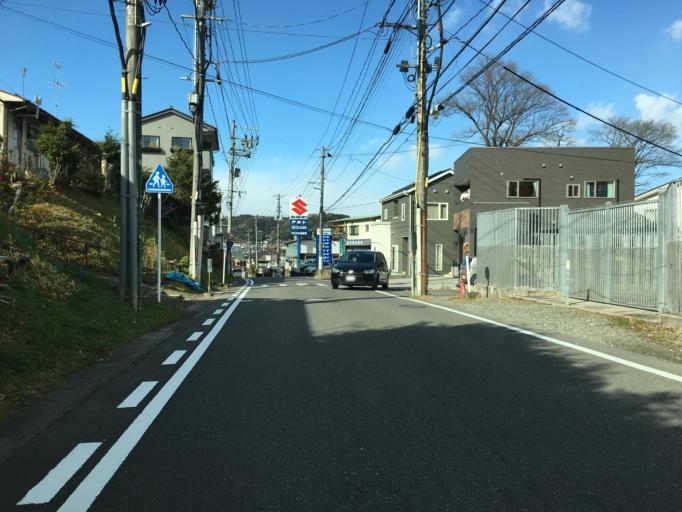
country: JP
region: Fukushima
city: Nihommatsu
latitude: 37.5970
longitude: 140.4512
